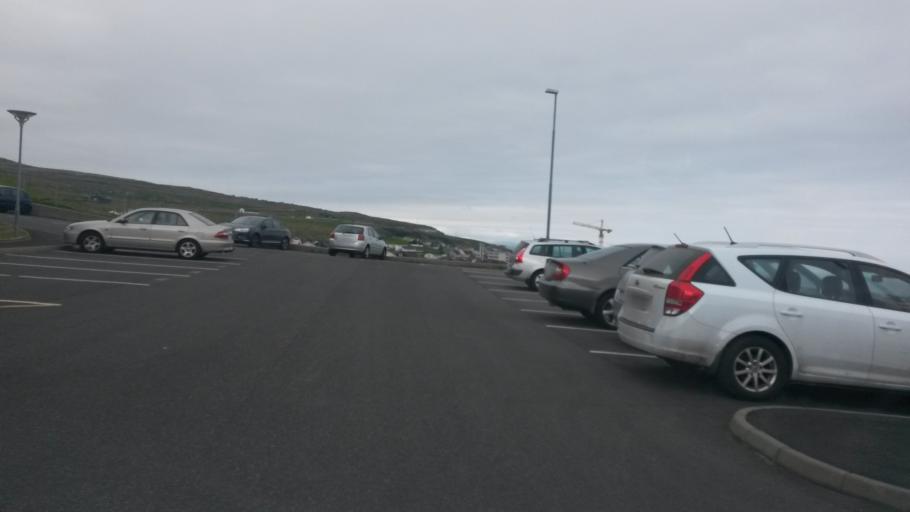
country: FO
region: Streymoy
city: Argir
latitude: 62.0021
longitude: -6.8061
